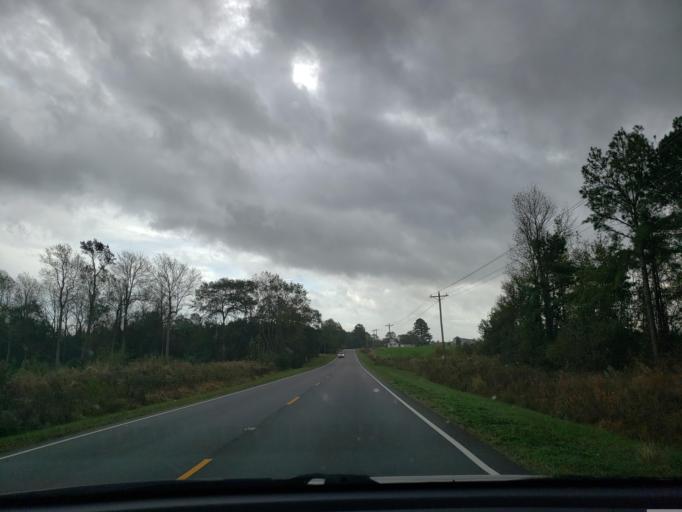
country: US
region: North Carolina
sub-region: Duplin County
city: Beulaville
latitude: 34.8595
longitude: -77.8774
